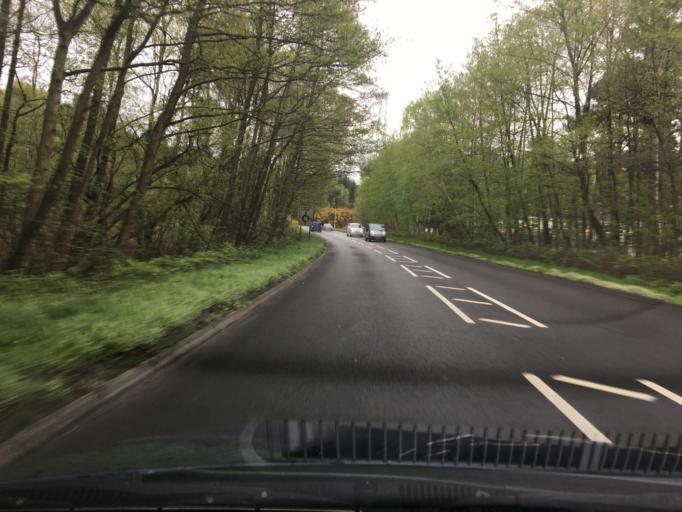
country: GB
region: England
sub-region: Bracknell Forest
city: Sandhurst
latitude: 51.3585
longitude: -0.7768
